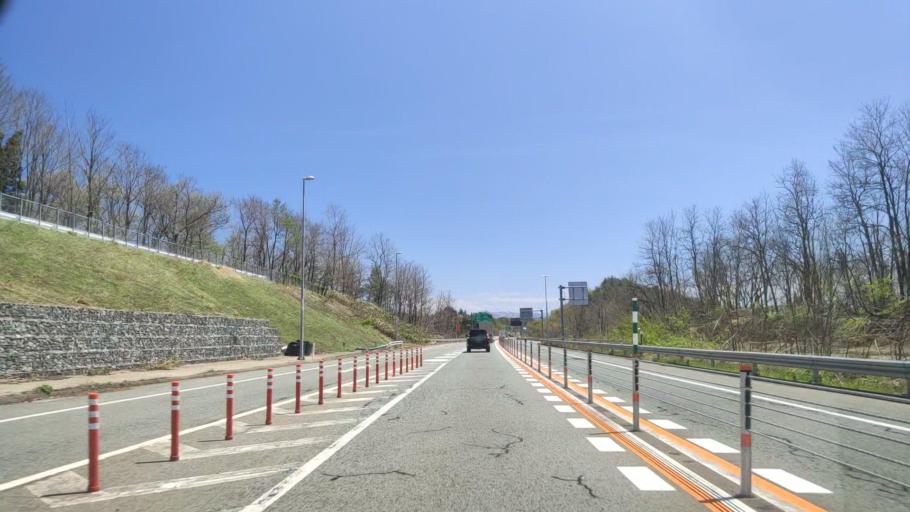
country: JP
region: Yamagata
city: Obanazawa
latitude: 38.6565
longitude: 140.3660
